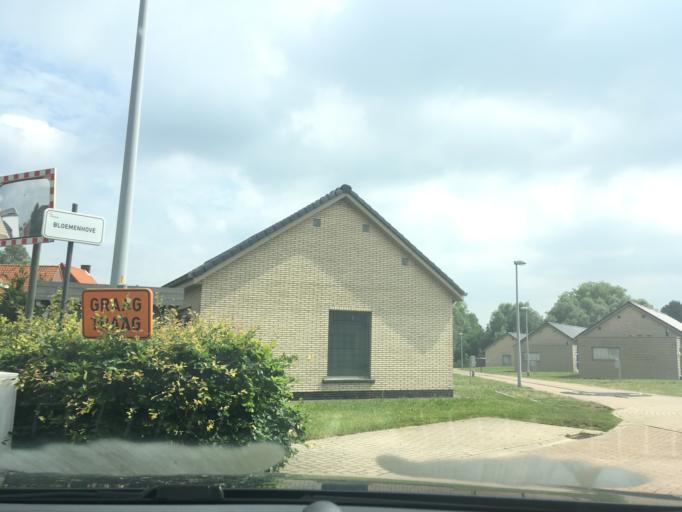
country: BE
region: Flanders
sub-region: Provincie West-Vlaanderen
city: Meulebeke
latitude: 50.9447
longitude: 3.2950
